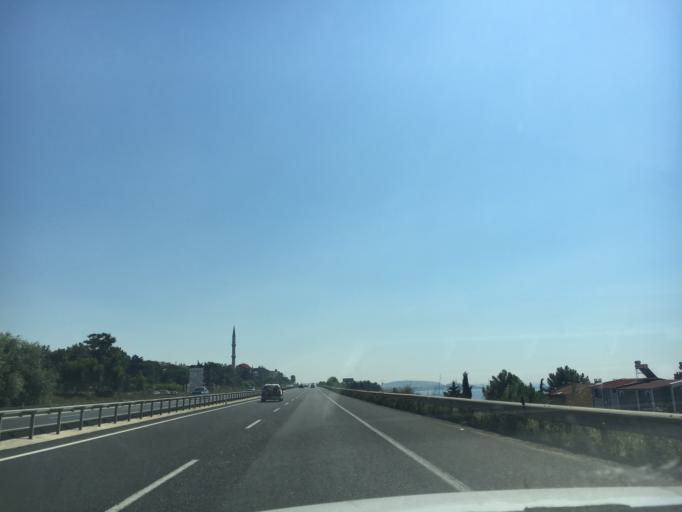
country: TR
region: Tekirdag
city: Marmara Ereglisi
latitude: 40.9690
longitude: 27.8976
